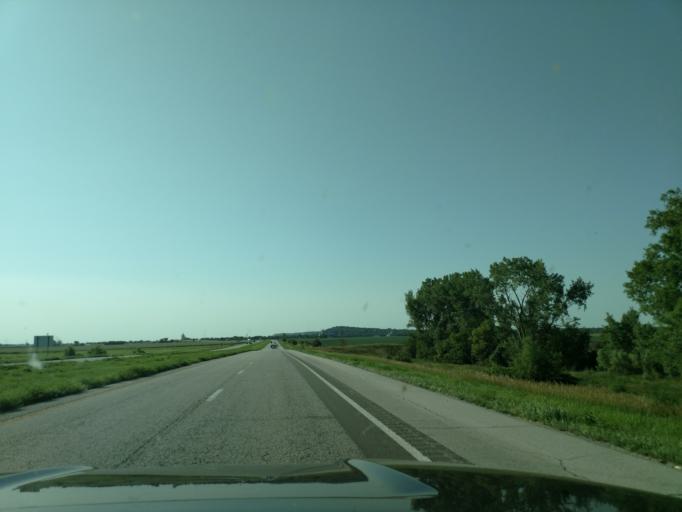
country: US
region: Iowa
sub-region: Fremont County
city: Hamburg
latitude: 40.5726
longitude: -95.6437
